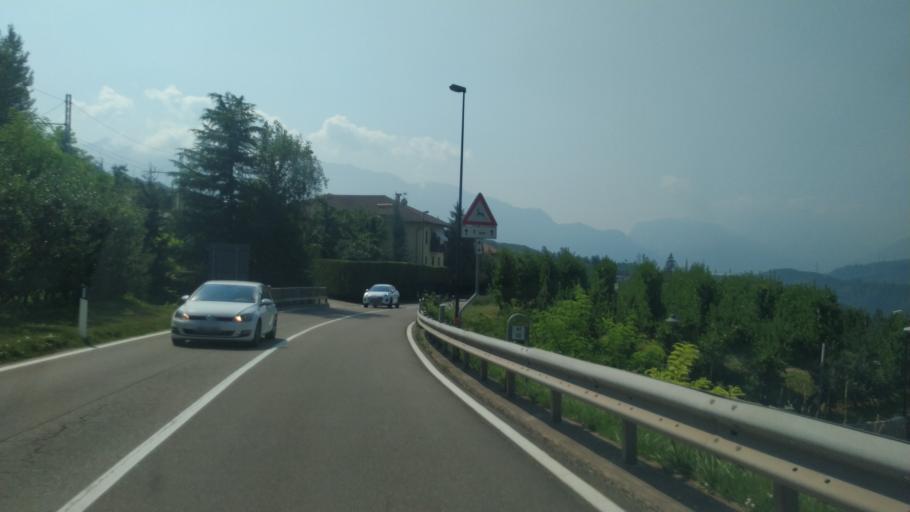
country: IT
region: Trentino-Alto Adige
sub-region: Provincia di Trento
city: Taio
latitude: 46.3347
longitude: 11.0635
